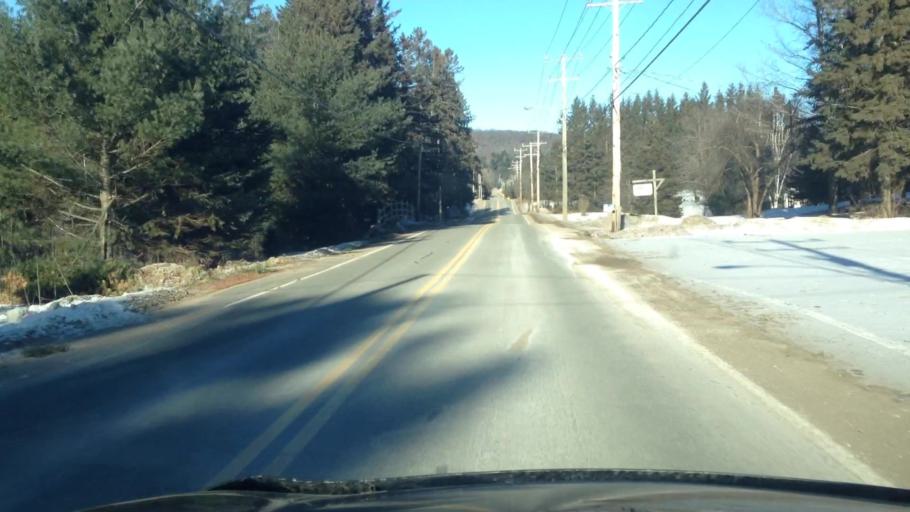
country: CA
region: Quebec
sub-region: Laurentides
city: Mont-Tremblant
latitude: 45.9793
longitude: -74.6131
